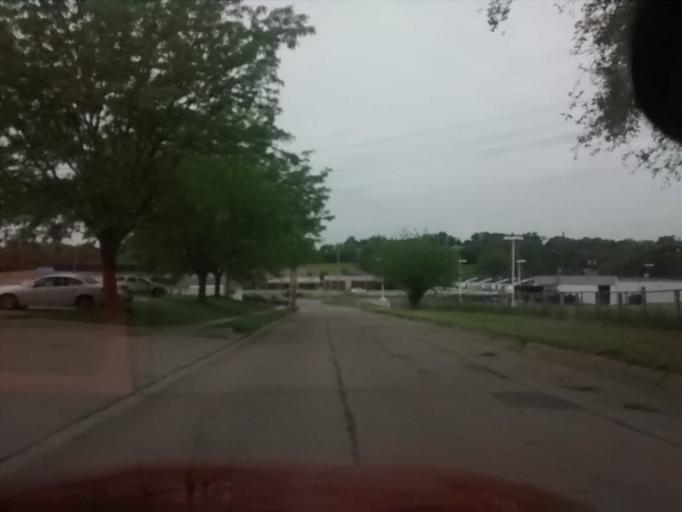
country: US
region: Nebraska
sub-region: Sarpy County
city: Bellevue
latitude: 41.1719
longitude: -95.9238
